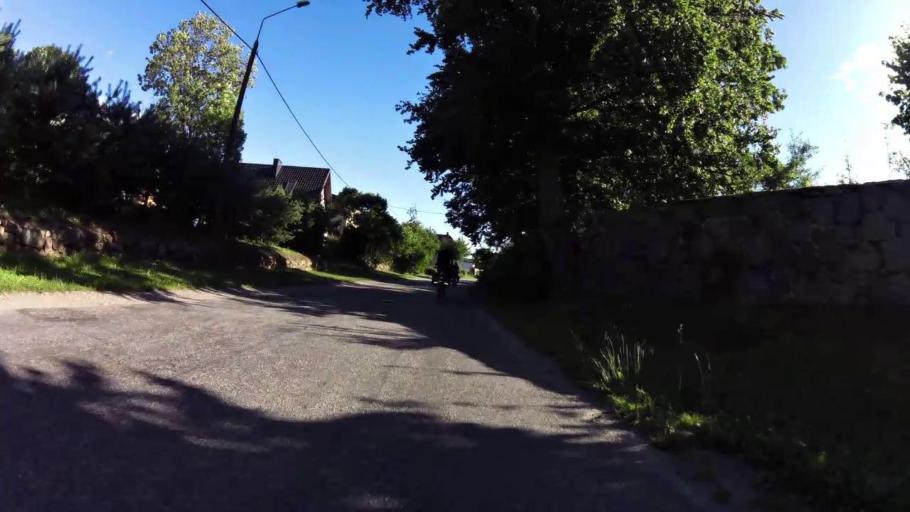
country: PL
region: West Pomeranian Voivodeship
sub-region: Powiat swidwinski
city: Swidwin
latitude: 53.7735
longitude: 15.7408
